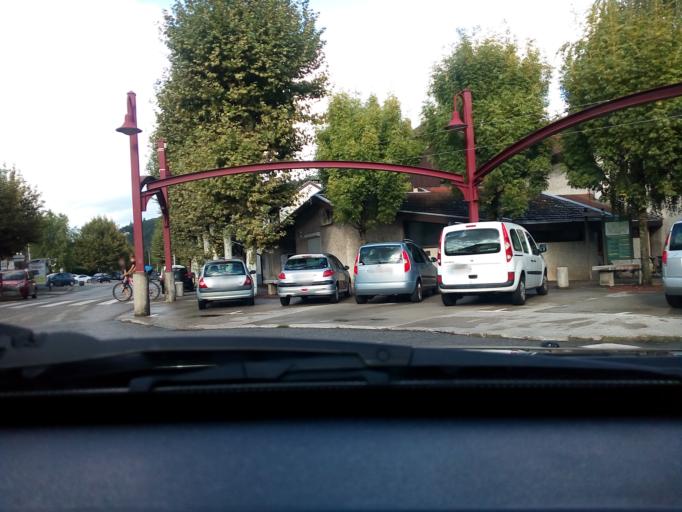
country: FR
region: Rhone-Alpes
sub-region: Departement de l'Isere
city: Poisat
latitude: 45.1586
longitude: 5.7591
